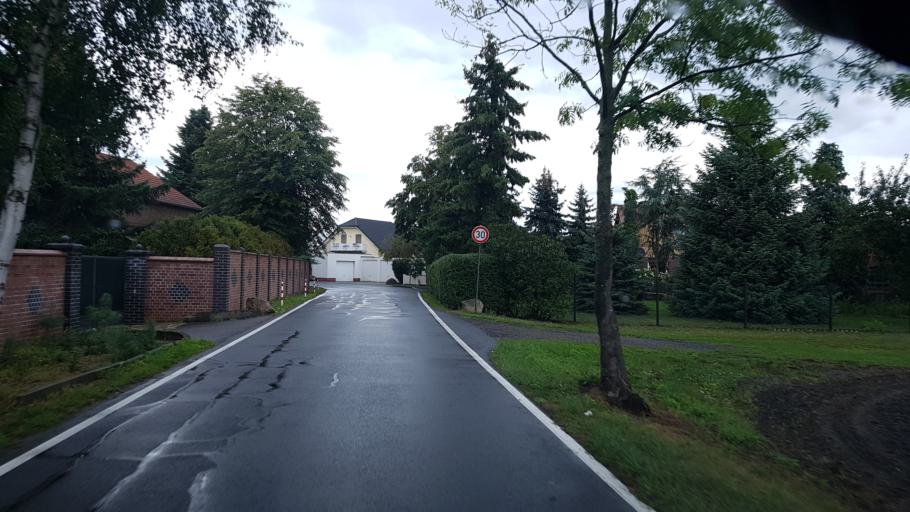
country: DE
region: Brandenburg
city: Grossraschen
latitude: 51.5864
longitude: 14.0390
